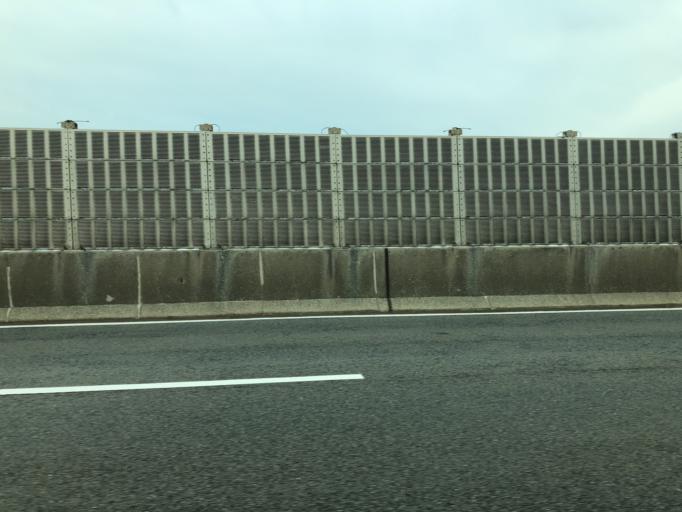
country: JP
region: Hyogo
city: Ashiya
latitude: 34.7079
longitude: 135.2800
